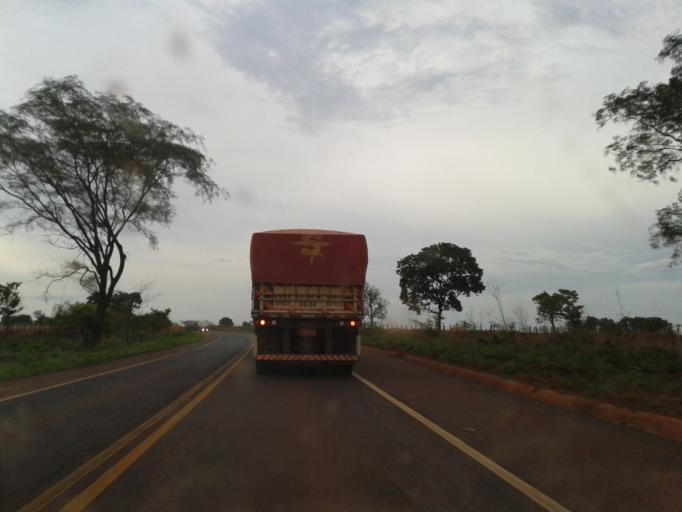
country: BR
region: Goias
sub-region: Santa Helena De Goias
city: Santa Helena de Goias
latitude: -17.9488
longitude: -50.5122
